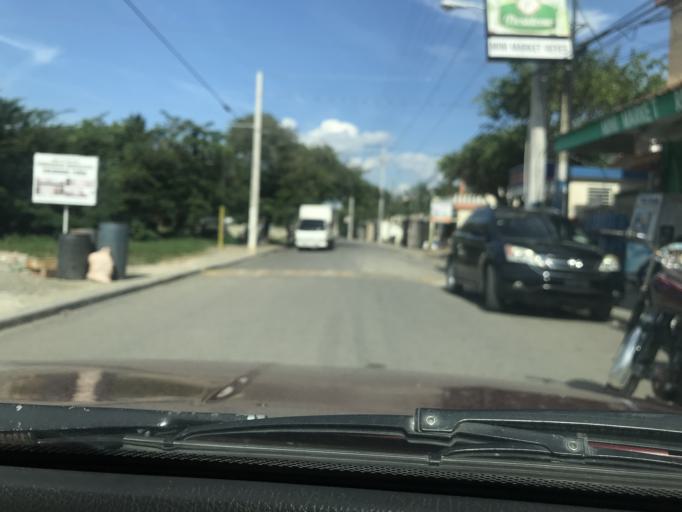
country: DO
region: Santiago
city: Licey al Medio
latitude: 19.4058
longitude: -70.6292
